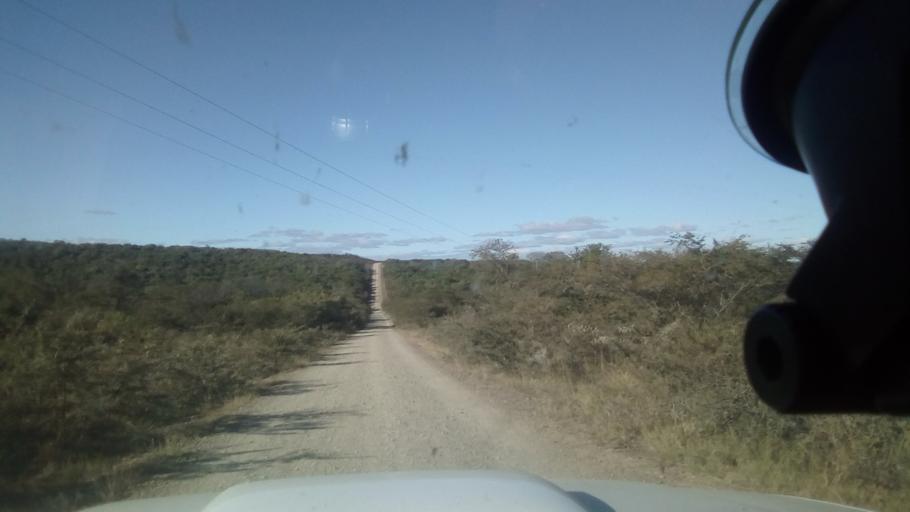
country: ZA
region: Eastern Cape
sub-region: Buffalo City Metropolitan Municipality
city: Bhisho
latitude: -32.7531
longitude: 27.3396
